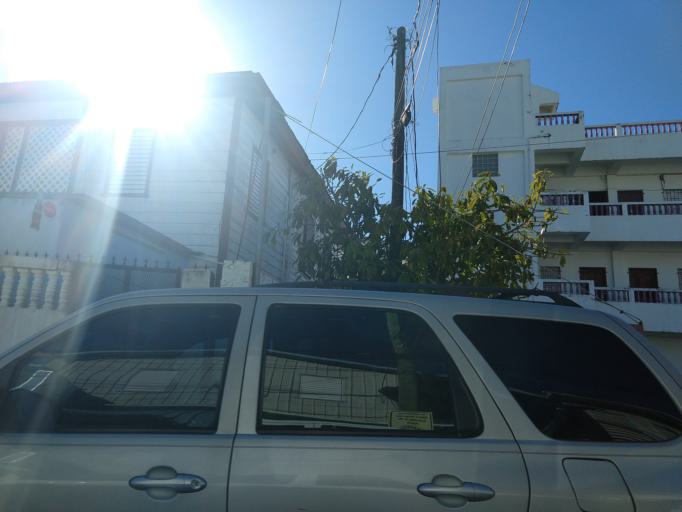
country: BZ
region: Belize
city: Belize City
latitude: 17.4979
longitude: -88.1841
